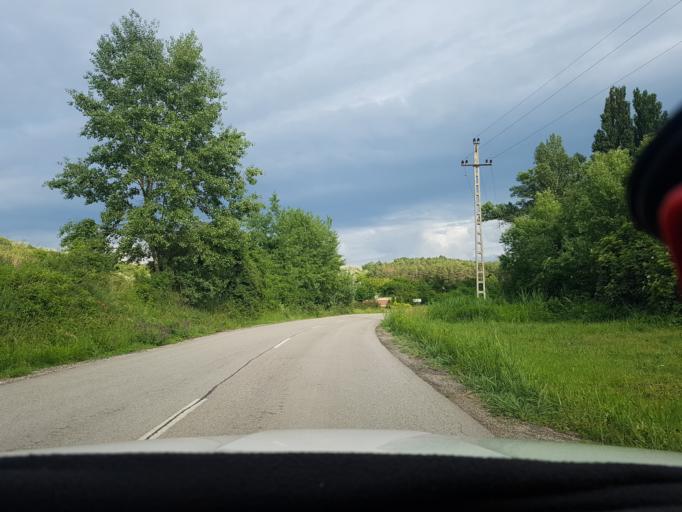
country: HU
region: Komarom-Esztergom
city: Labatlan
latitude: 47.7385
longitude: 18.5204
